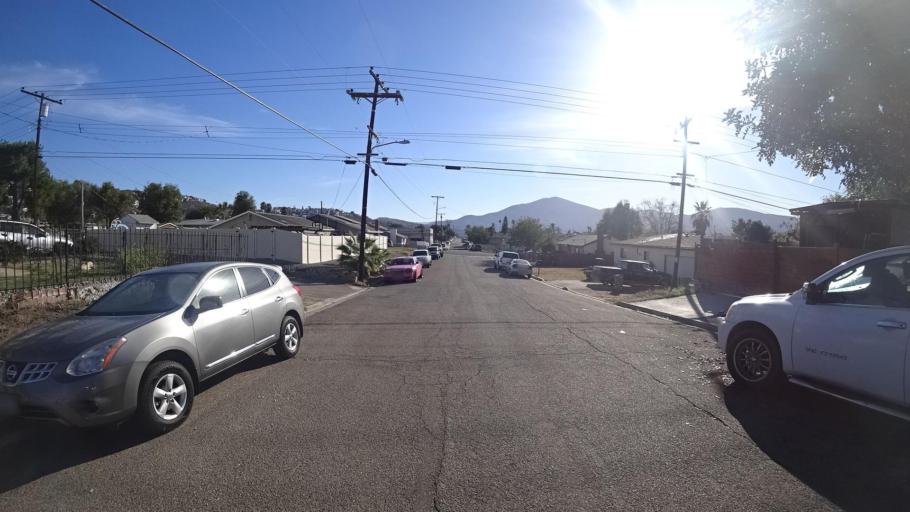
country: US
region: California
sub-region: San Diego County
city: La Presa
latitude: 32.7117
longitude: -116.9995
